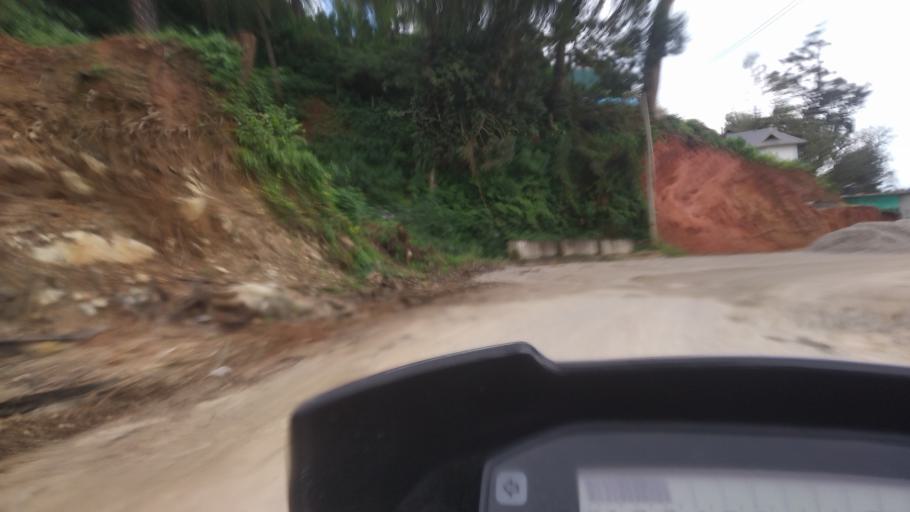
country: IN
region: Kerala
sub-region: Idukki
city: Munnar
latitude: 10.0348
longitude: 77.1495
